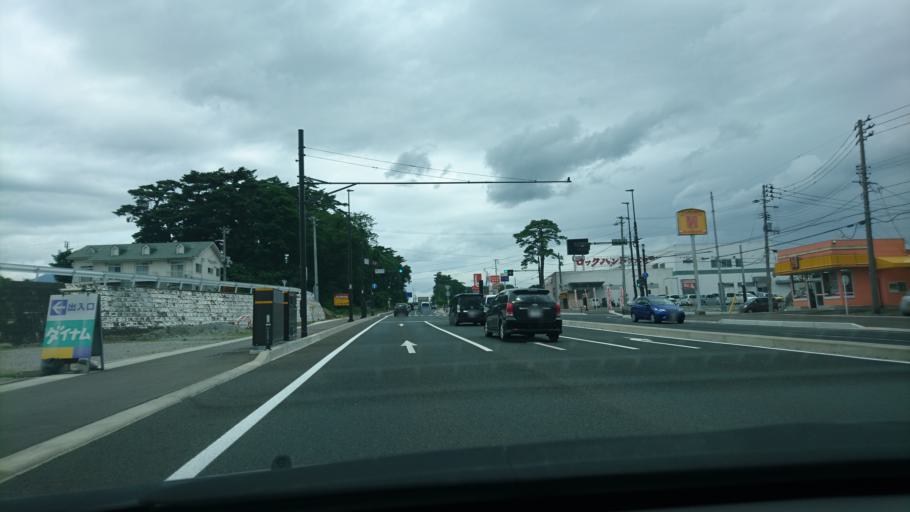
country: JP
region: Iwate
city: Morioka-shi
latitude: 39.7719
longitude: 141.1292
